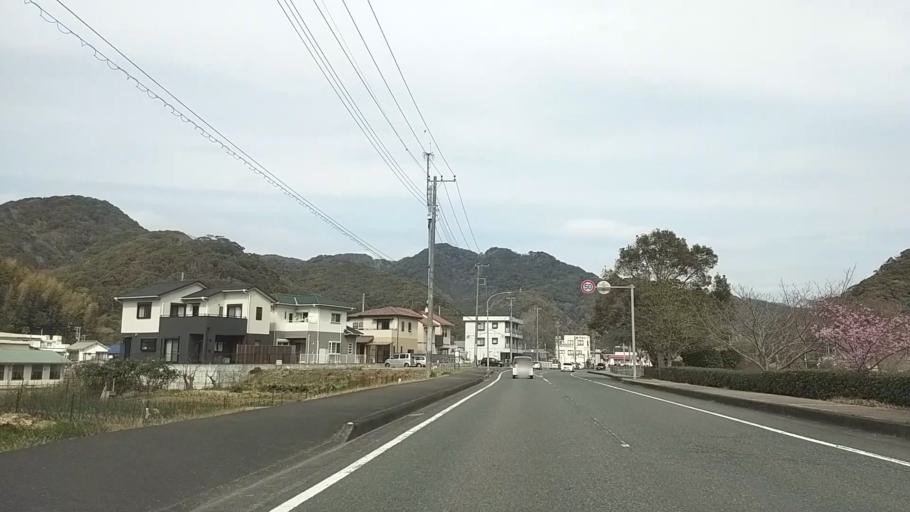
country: JP
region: Shizuoka
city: Shimoda
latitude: 34.6979
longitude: 138.9401
